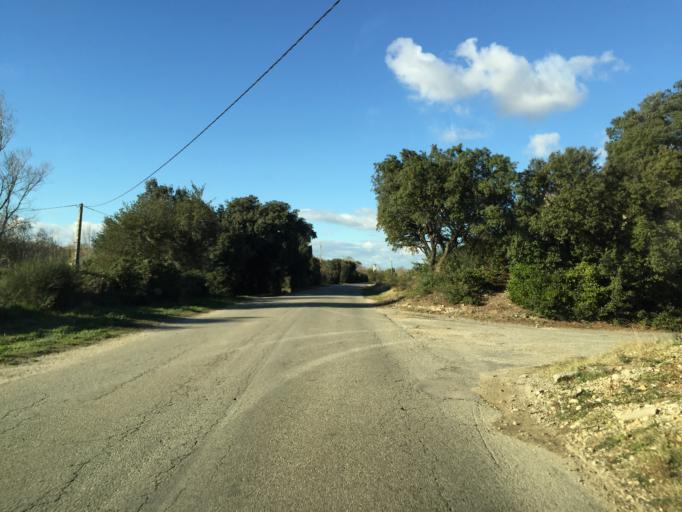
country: FR
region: Provence-Alpes-Cote d'Azur
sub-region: Departement du Vaucluse
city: Sorgues
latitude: 44.0187
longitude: 4.8491
